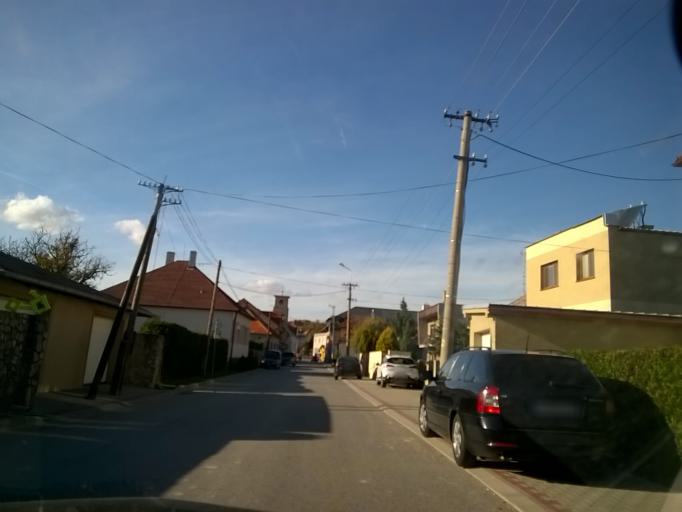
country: SK
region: Nitriansky
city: Zlate Moravce
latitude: 48.4182
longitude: 18.4139
